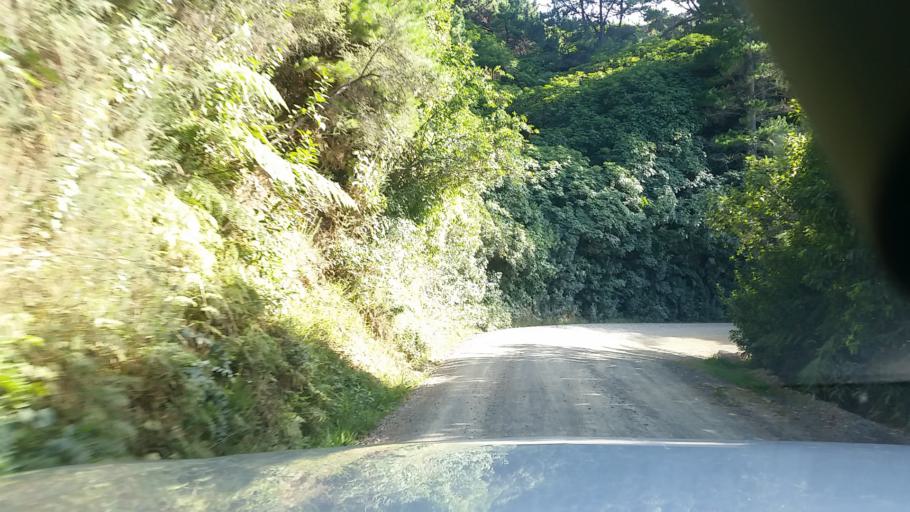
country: NZ
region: Marlborough
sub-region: Marlborough District
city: Picton
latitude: -41.2964
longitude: 174.1237
